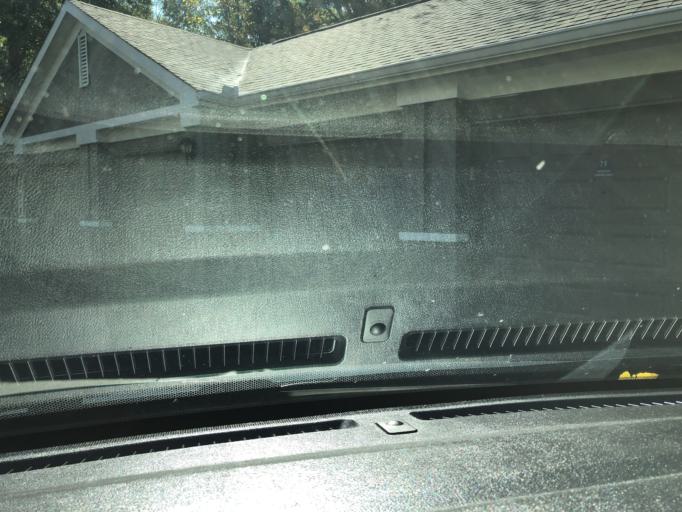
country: US
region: Georgia
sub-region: Fulton County
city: Johns Creek
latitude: 34.0168
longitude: -84.1834
